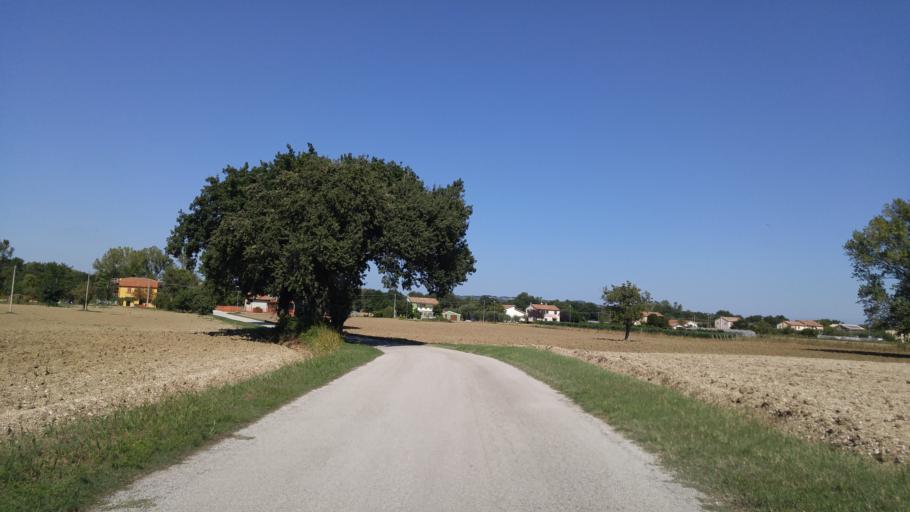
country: IT
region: The Marches
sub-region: Provincia di Pesaro e Urbino
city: Villanova
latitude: 43.7504
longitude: 12.9376
